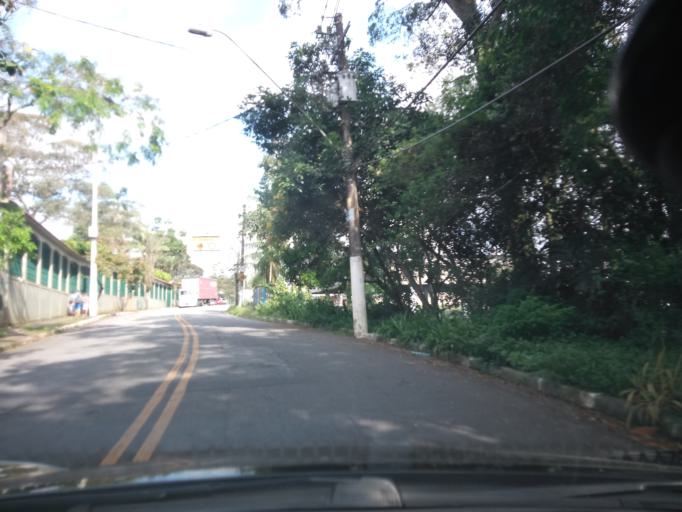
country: BR
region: Sao Paulo
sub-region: Sao Bernardo Do Campo
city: Sao Bernardo do Campo
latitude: -23.7859
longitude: -46.5382
